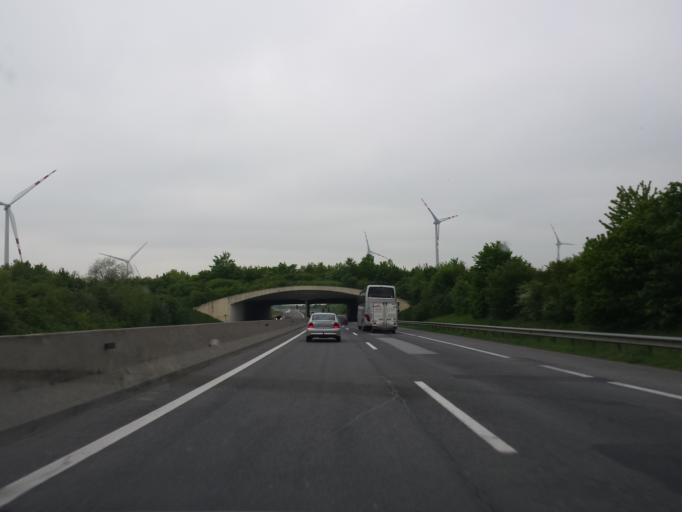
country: AT
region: Burgenland
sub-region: Politischer Bezirk Neusiedl am See
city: Zurndorf
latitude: 47.9379
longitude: 16.9809
